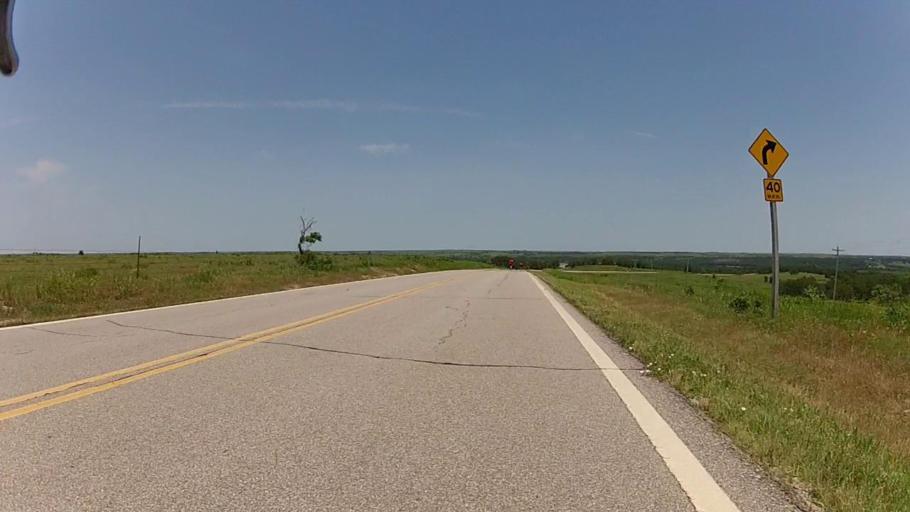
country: US
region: Kansas
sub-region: Chautauqua County
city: Sedan
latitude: 37.1130
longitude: -96.2431
